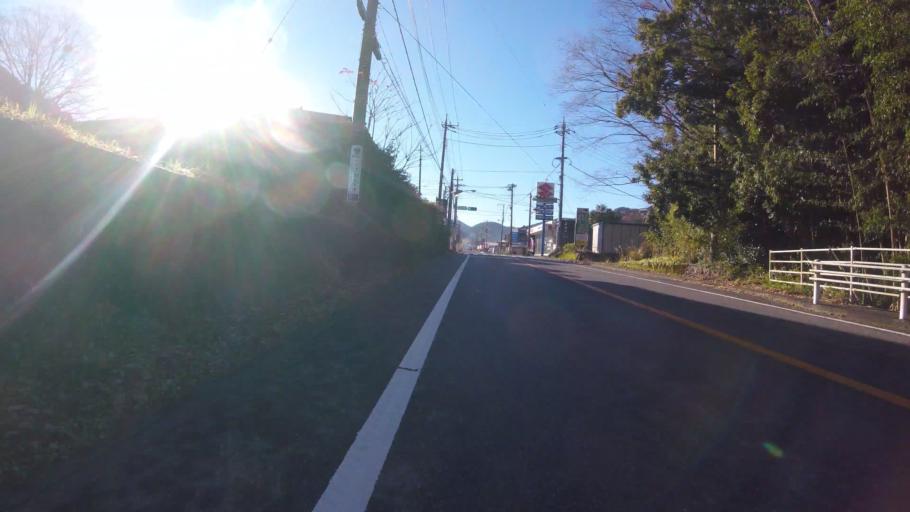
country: JP
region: Shizuoka
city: Heda
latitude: 34.9099
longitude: 138.9242
